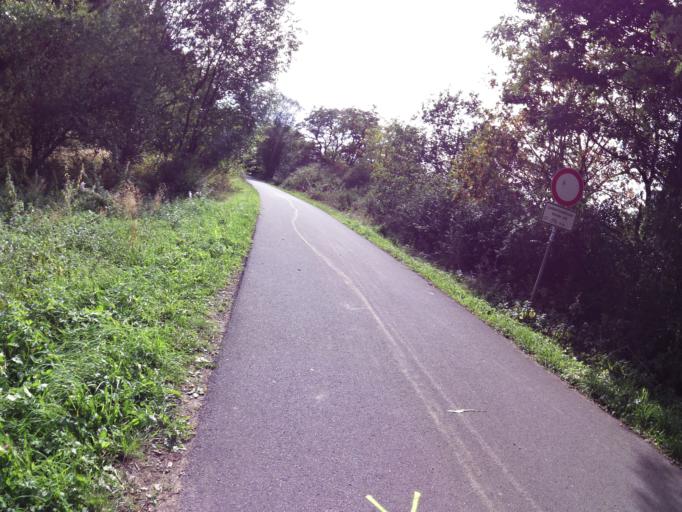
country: DE
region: Rheinland-Pfalz
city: Winterscheid
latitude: 50.2343
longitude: 6.2619
